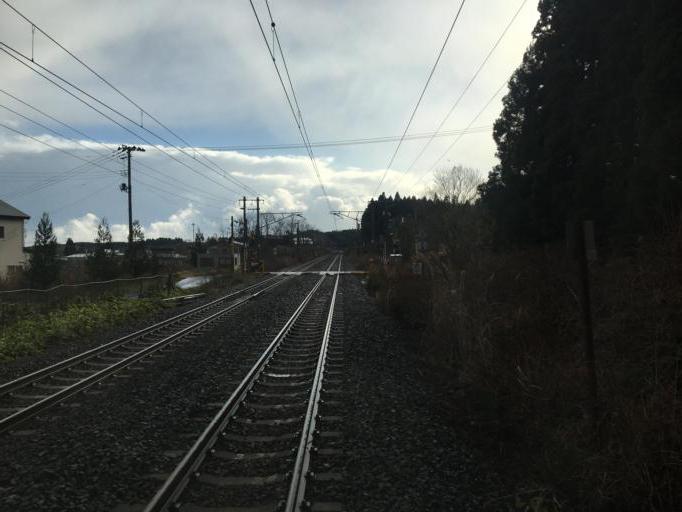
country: JP
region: Aomori
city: Aomori Shi
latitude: 40.9175
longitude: 141.0322
